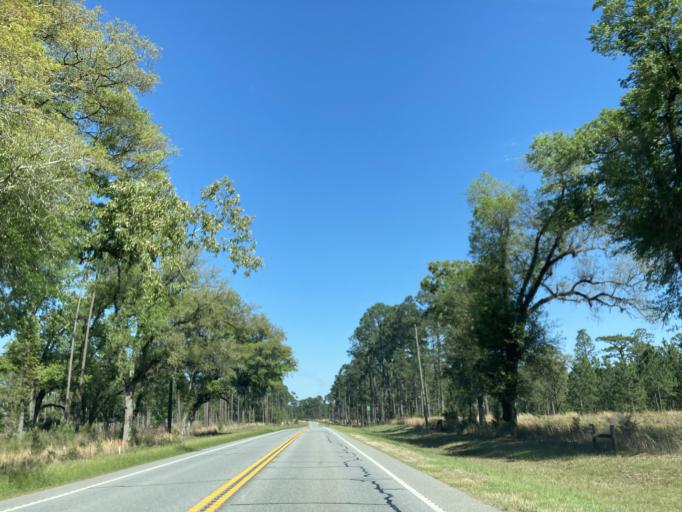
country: US
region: Georgia
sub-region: Baker County
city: Newton
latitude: 31.2132
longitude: -84.4661
